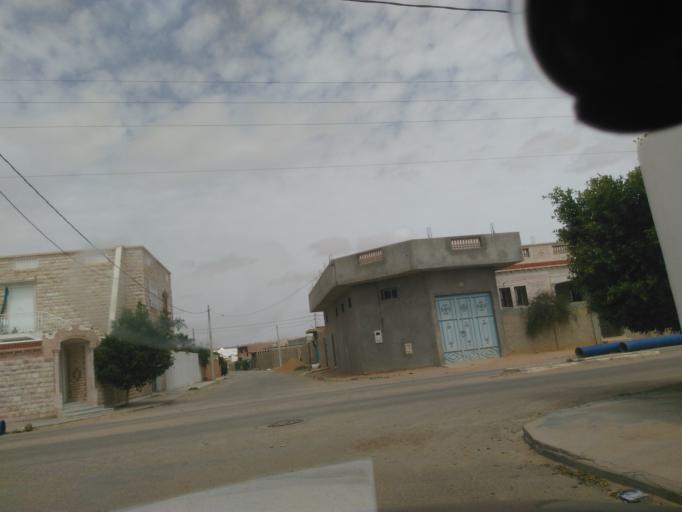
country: TN
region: Tataouine
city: Tataouine
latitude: 32.9480
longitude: 10.4689
